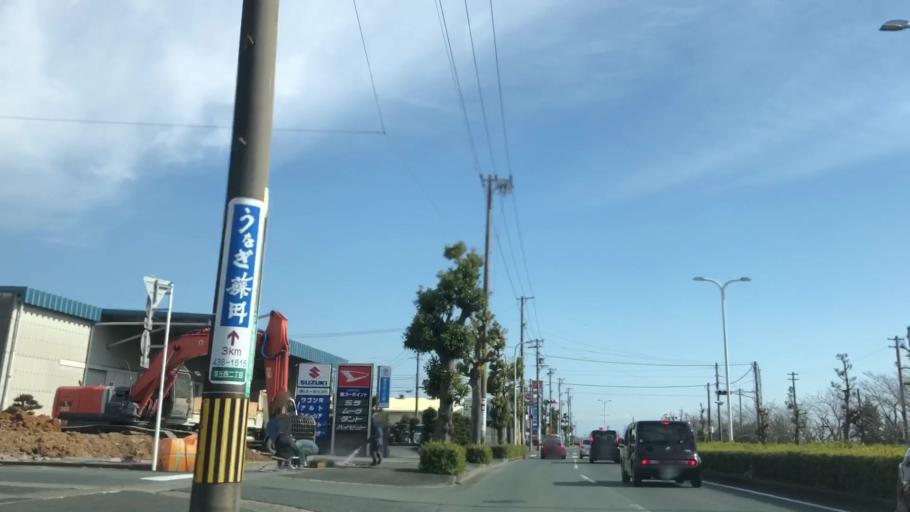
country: JP
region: Shizuoka
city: Hamamatsu
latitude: 34.7550
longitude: 137.6974
